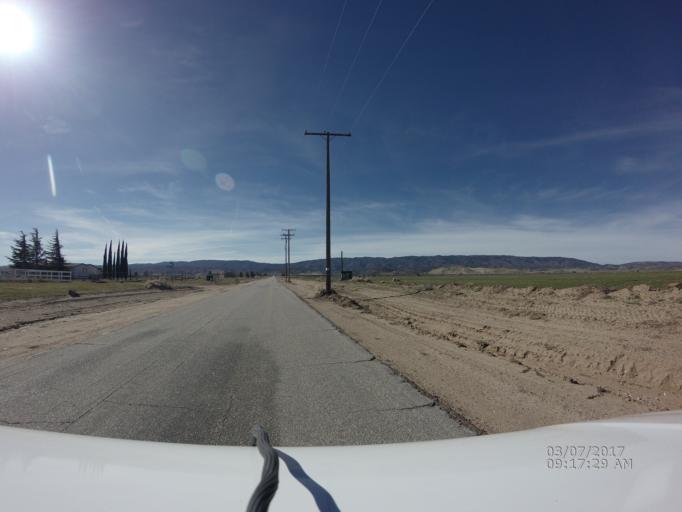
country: US
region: California
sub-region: Los Angeles County
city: Green Valley
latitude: 34.7931
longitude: -118.5900
